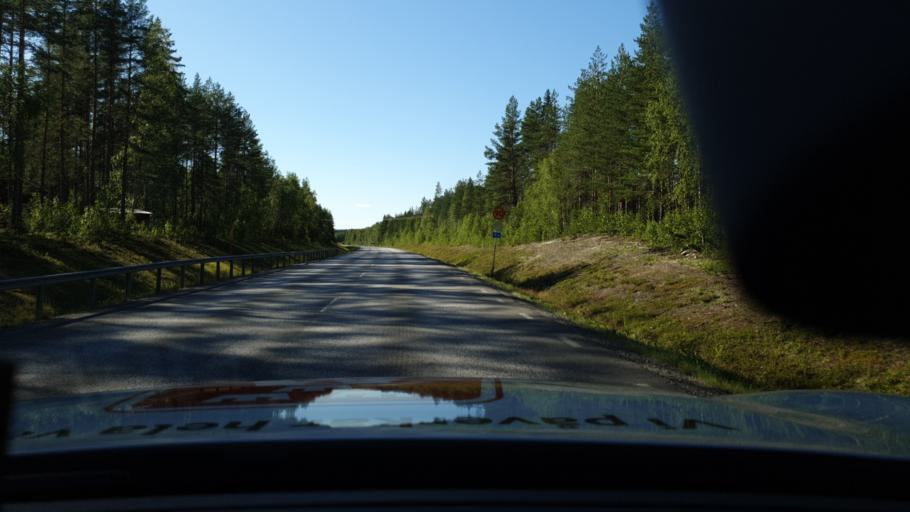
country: SE
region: Norrbotten
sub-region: Pitea Kommun
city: Rosvik
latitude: 65.5912
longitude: 21.6538
